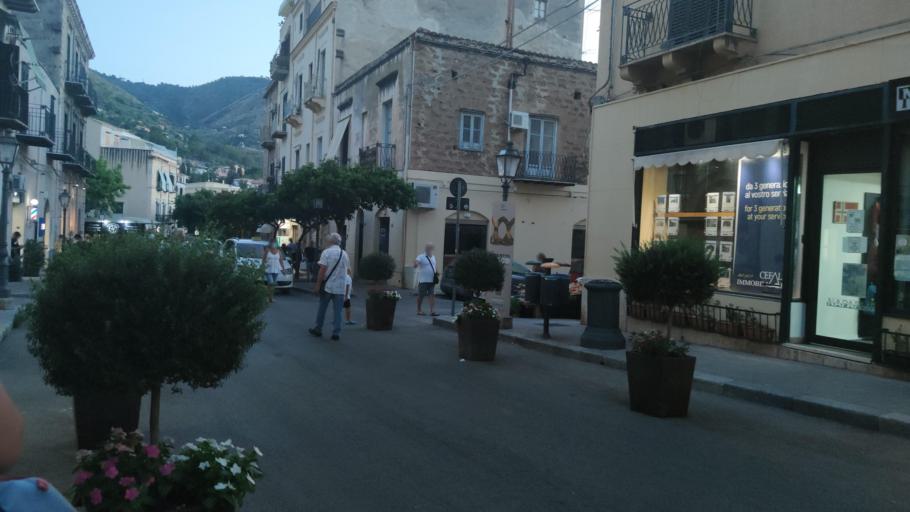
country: IT
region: Sicily
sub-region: Palermo
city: Cefalu
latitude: 38.0362
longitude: 14.0218
